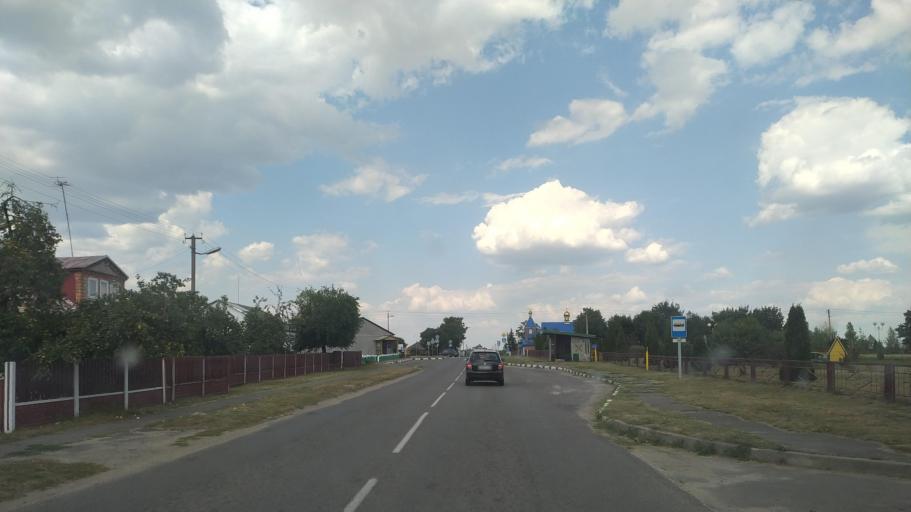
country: BY
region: Brest
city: Drahichyn
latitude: 52.1152
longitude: 25.1160
